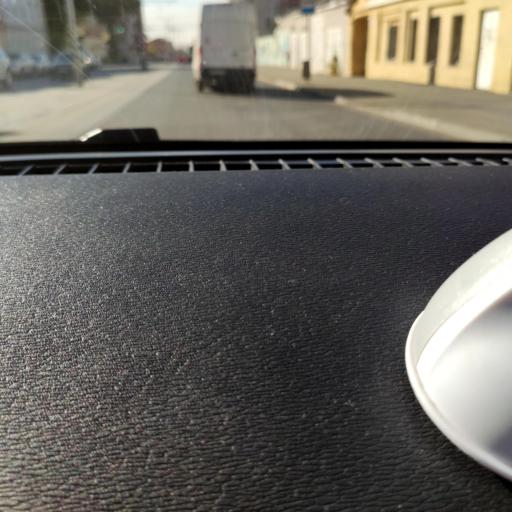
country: RU
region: Samara
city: Samara
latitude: 53.1889
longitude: 50.1001
